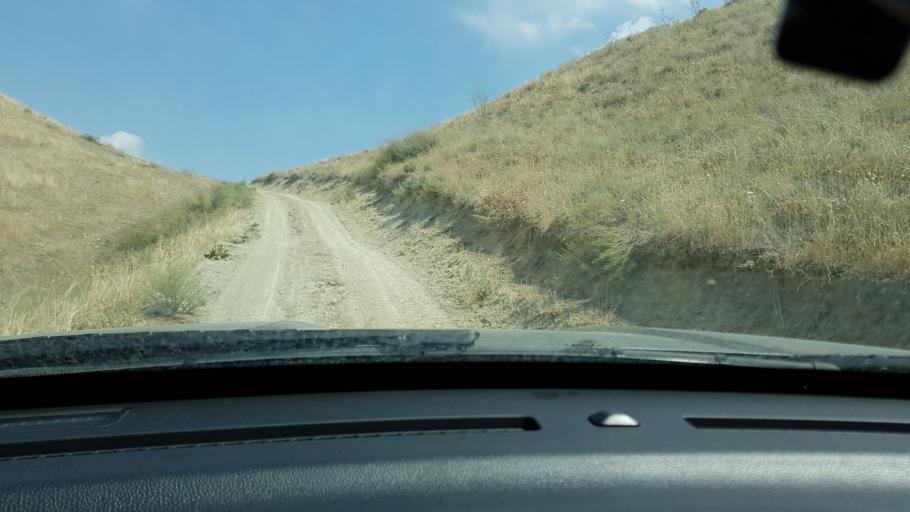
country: TM
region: Ahal
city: Baharly
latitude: 38.4049
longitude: 56.9078
